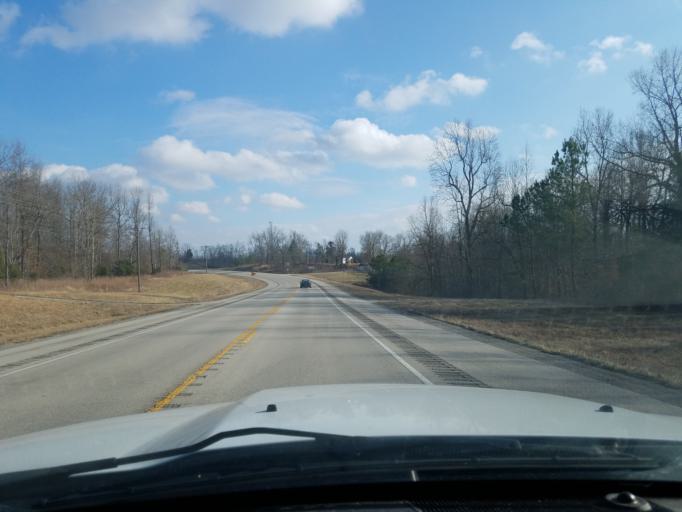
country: US
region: Kentucky
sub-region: Larue County
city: Hodgenville
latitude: 37.4673
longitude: -85.5817
